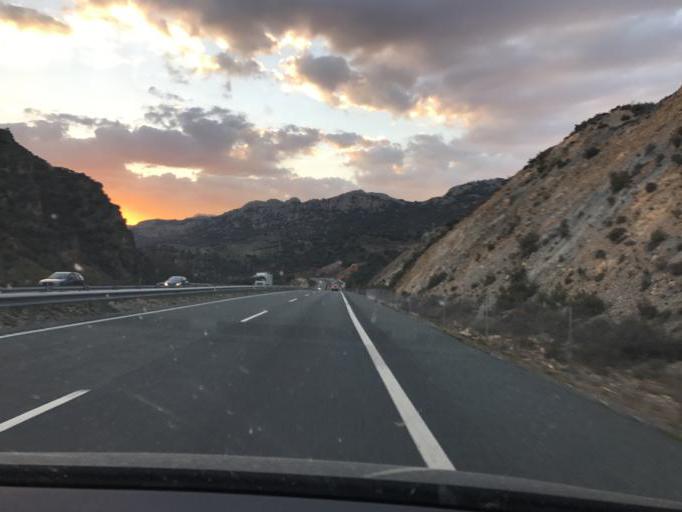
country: ES
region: Andalusia
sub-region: Provincia de Granada
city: Diezma
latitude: 37.3115
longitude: -3.3812
